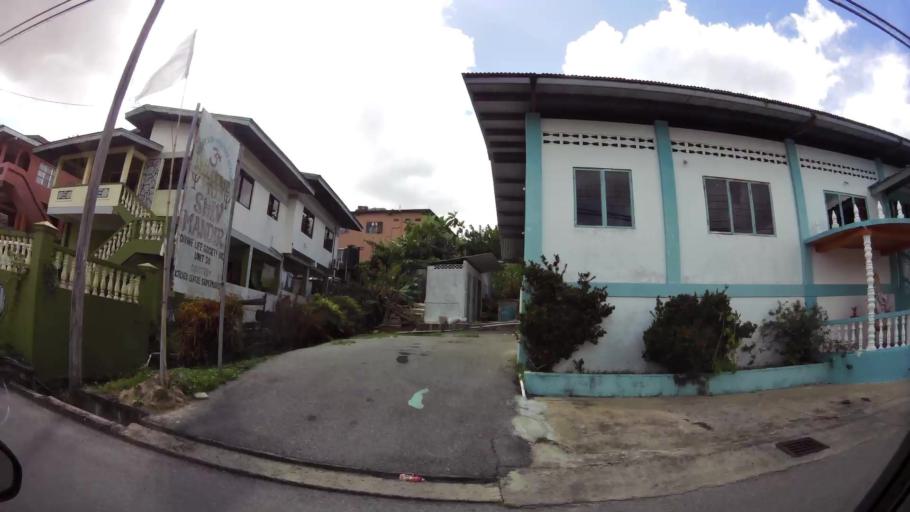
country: TT
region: Penal/Debe
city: Debe
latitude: 10.2333
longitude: -61.4406
